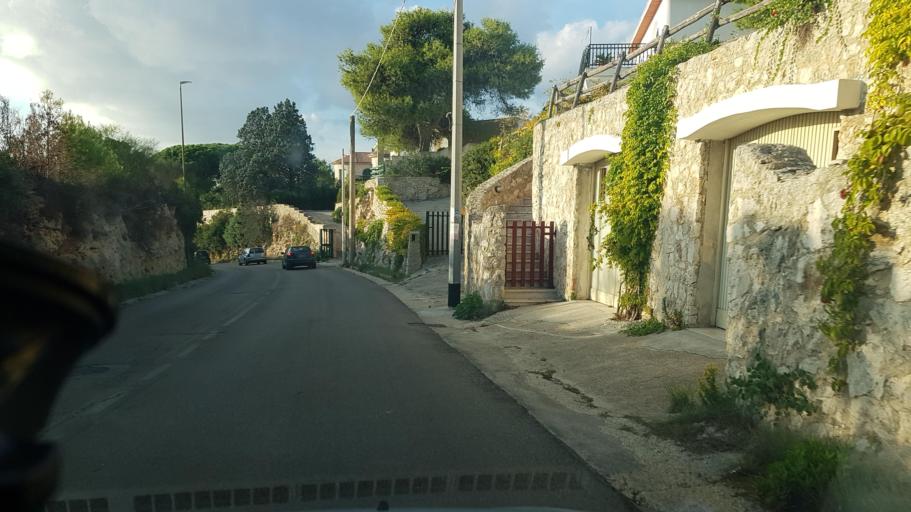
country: IT
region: Apulia
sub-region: Provincia di Lecce
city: Leuca
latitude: 39.7998
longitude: 18.3673
